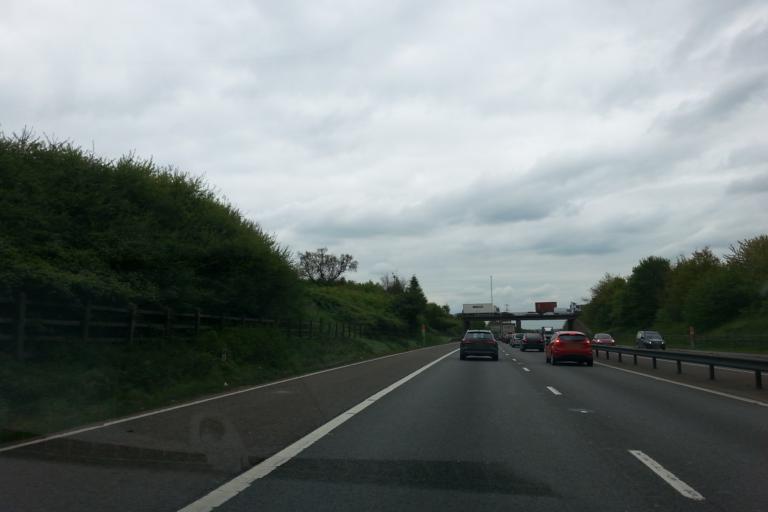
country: GB
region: England
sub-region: Warwickshire
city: Curdworth
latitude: 52.5382
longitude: -1.7268
